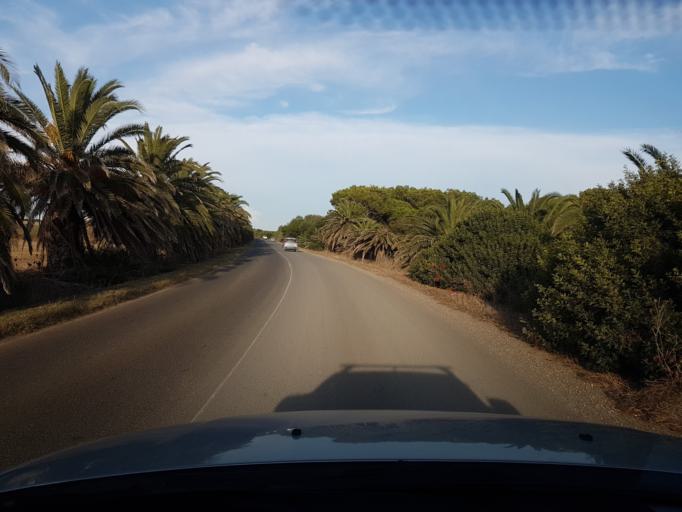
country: IT
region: Sardinia
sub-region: Provincia di Oristano
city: Cabras
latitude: 39.9497
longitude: 8.4127
